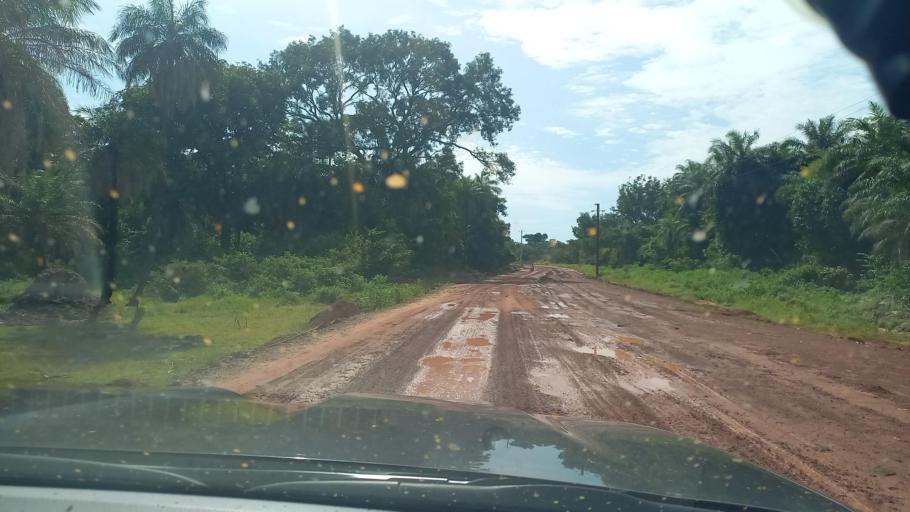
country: SN
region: Ziguinchor
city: Ziguinchor
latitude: 12.6724
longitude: -16.1908
